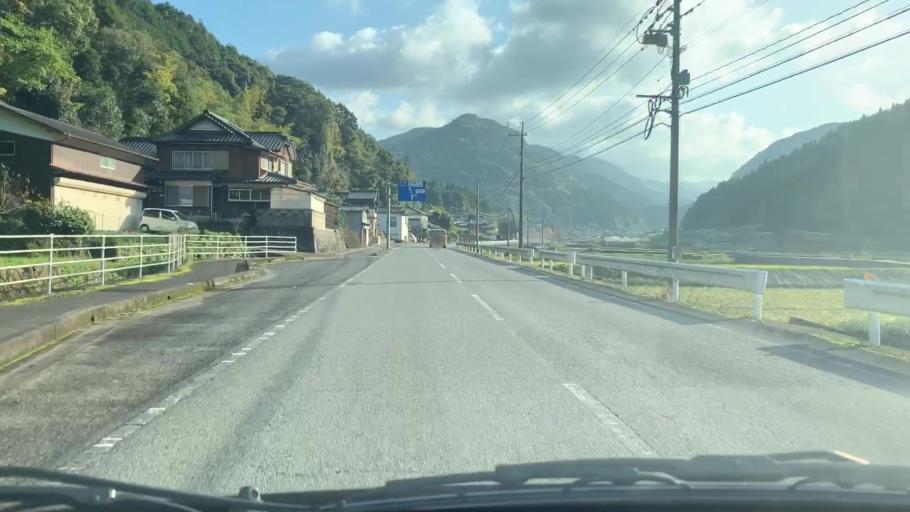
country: JP
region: Saga Prefecture
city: Kashima
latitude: 33.0591
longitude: 130.0701
